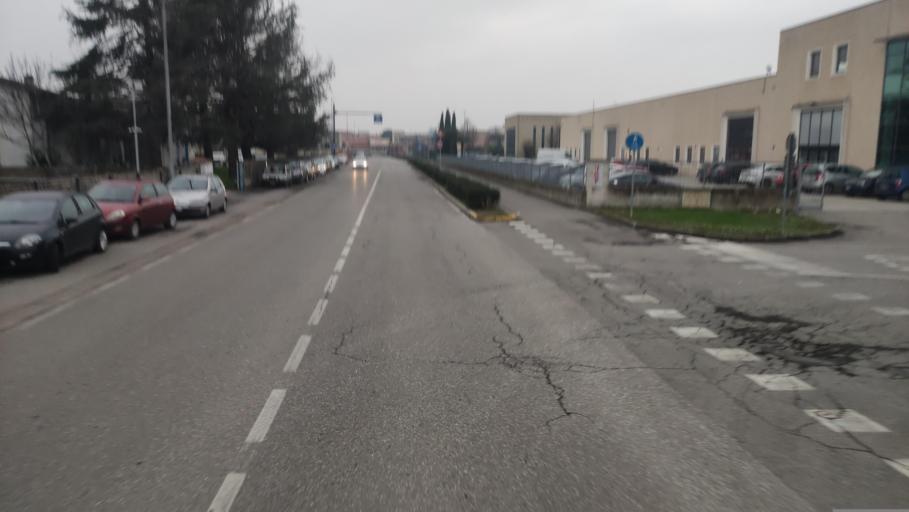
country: IT
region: Lombardy
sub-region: Provincia di Cremona
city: Bagnolo Cremasco
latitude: 45.3641
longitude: 9.6276
